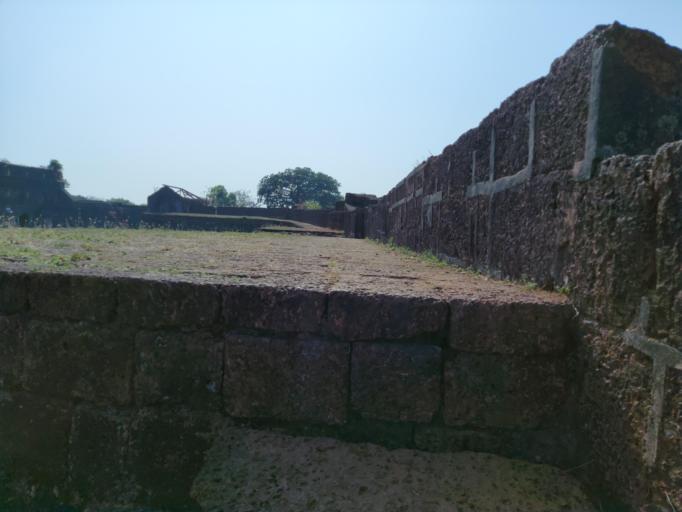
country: IN
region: Maharashtra
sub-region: Ratnagiri
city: Guhagar
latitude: 17.3007
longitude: 73.2208
